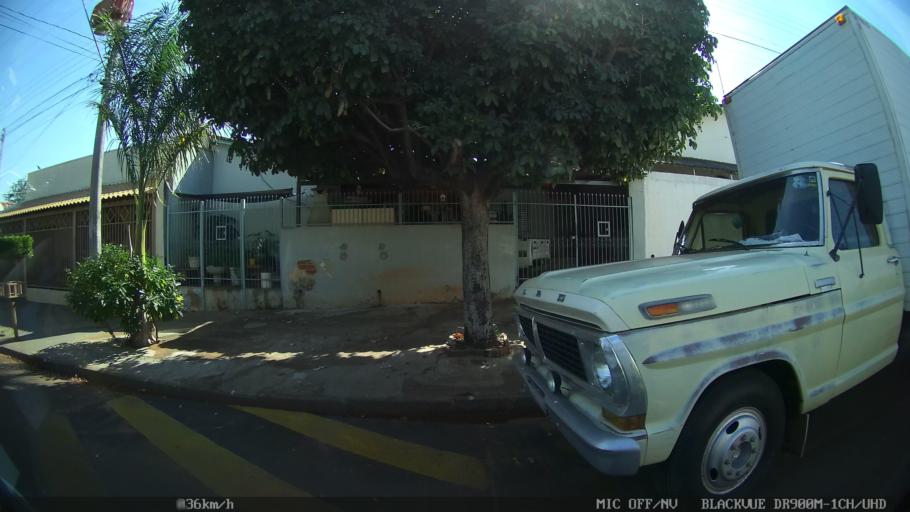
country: BR
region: Sao Paulo
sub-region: Sao Jose Do Rio Preto
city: Sao Jose do Rio Preto
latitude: -20.7865
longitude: -49.4015
